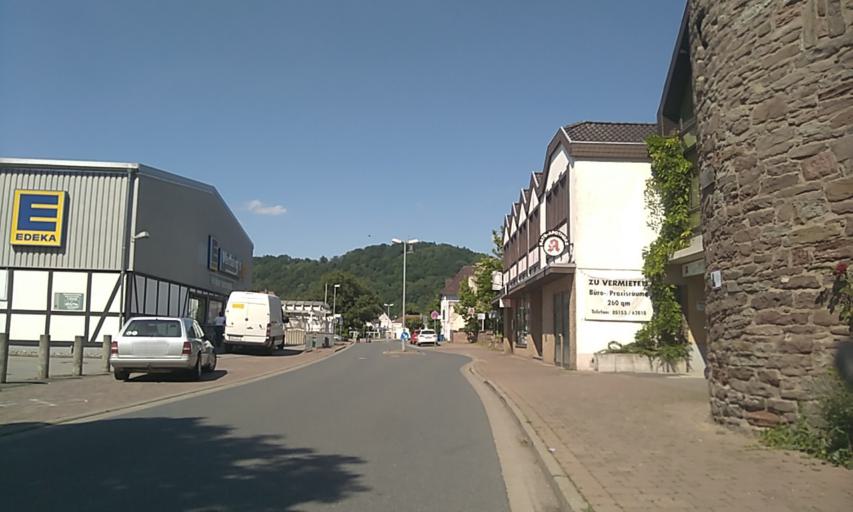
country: DE
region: Lower Saxony
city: Bodenwerder
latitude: 51.9778
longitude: 9.5149
